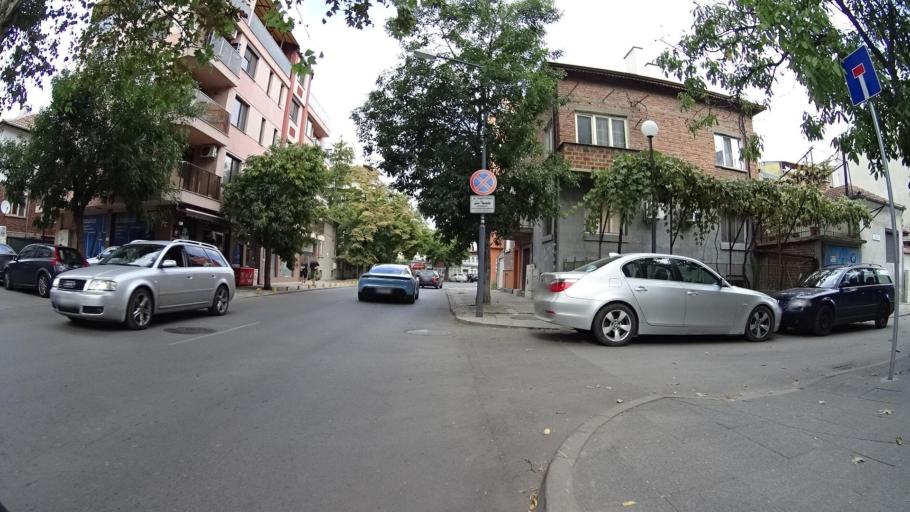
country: BG
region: Plovdiv
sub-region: Obshtina Plovdiv
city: Plovdiv
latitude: 42.1567
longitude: 24.7403
